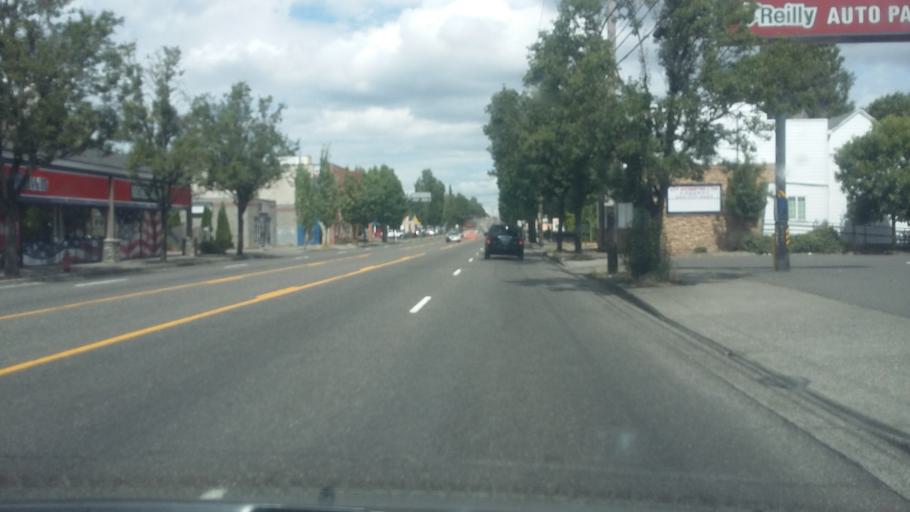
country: US
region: Oregon
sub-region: Multnomah County
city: Lents
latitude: 45.4986
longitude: -122.5787
